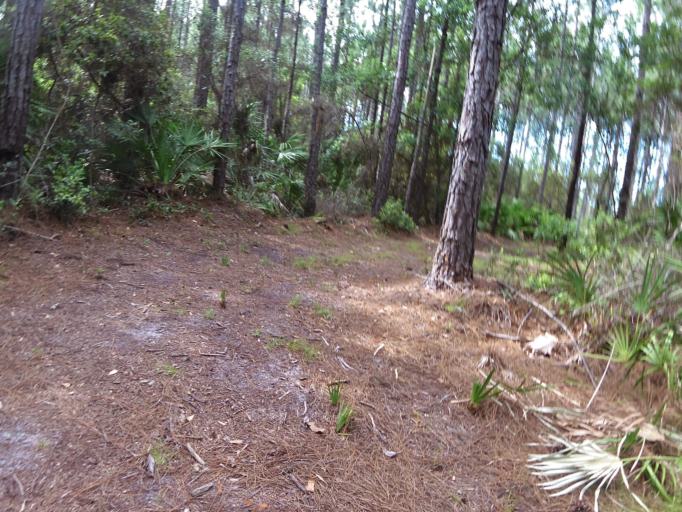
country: US
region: Florida
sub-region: Duval County
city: Atlantic Beach
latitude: 30.4563
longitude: -81.4715
